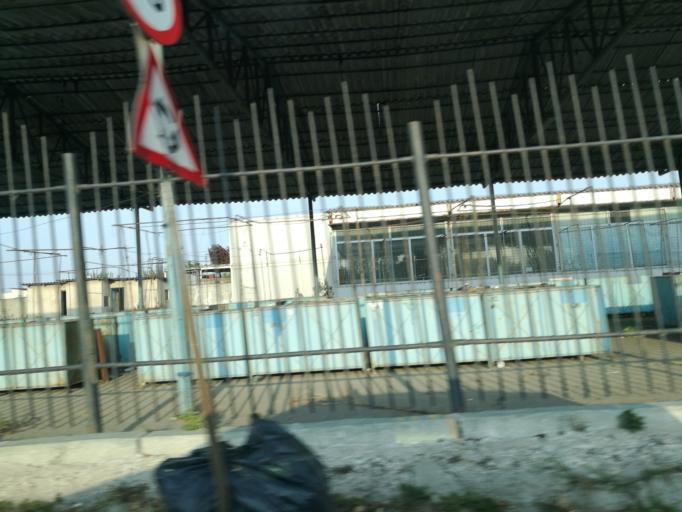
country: RO
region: Constanta
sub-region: Municipiul Constanta
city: Palazu Mare
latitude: 44.2037
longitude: 28.6106
